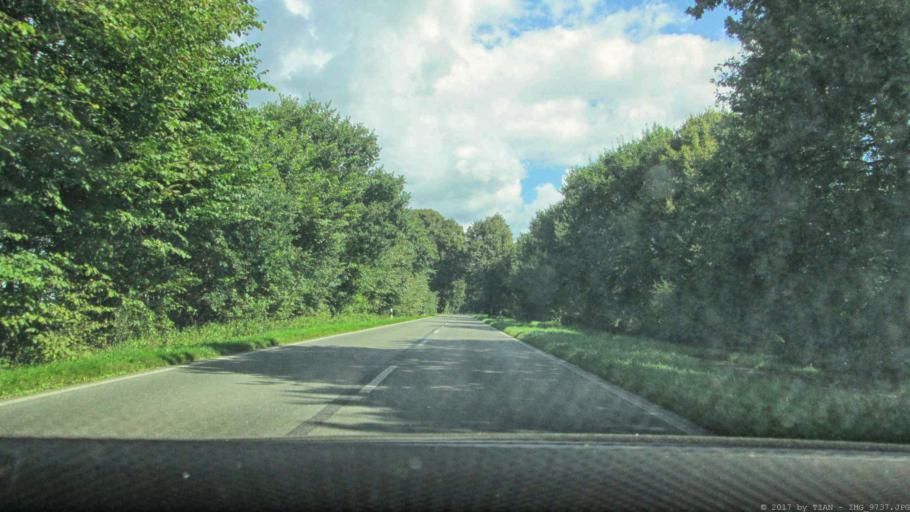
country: DE
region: Schleswig-Holstein
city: Kayhude
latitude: 53.7603
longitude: 10.1596
